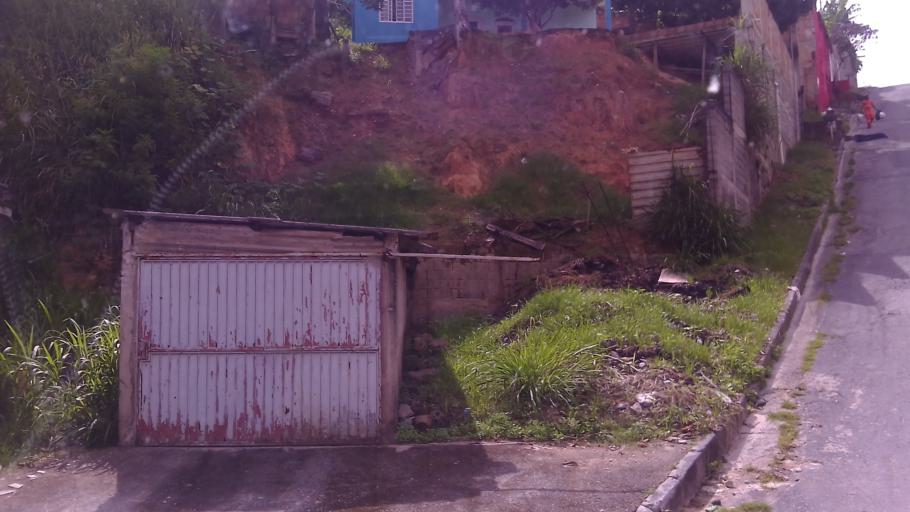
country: BR
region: Minas Gerais
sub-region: Santa Luzia
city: Santa Luzia
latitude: -19.8365
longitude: -43.8931
